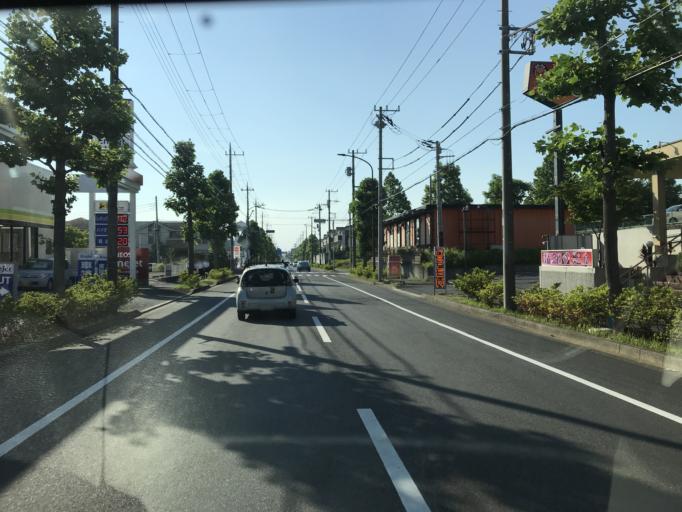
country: JP
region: Chiba
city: Chiba
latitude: 35.5433
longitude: 140.1841
